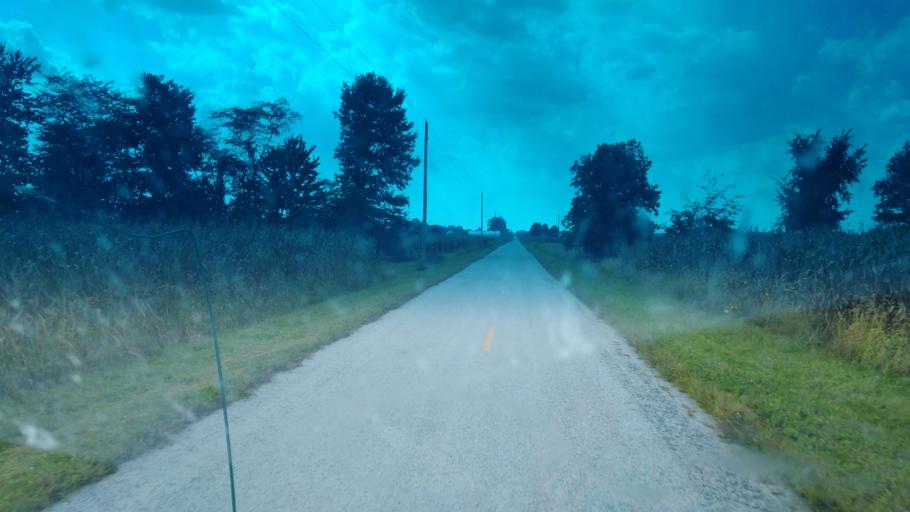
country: US
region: Ohio
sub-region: Hardin County
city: Kenton
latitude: 40.7178
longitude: -83.6039
